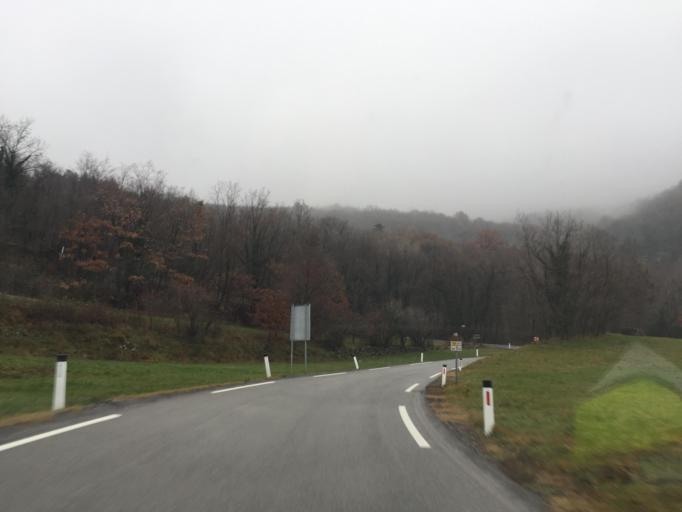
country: SI
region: Ajdovscina
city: Lokavec
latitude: 45.9160
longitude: 13.8932
